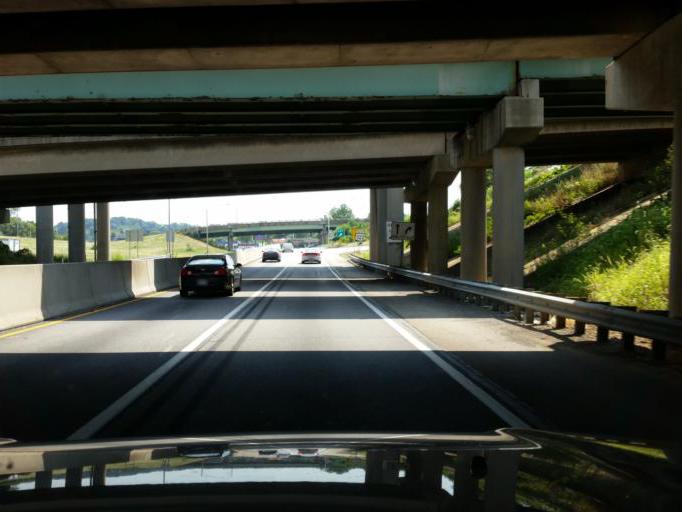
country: US
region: Pennsylvania
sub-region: Dauphin County
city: Lawnton
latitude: 40.2536
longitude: -76.8140
